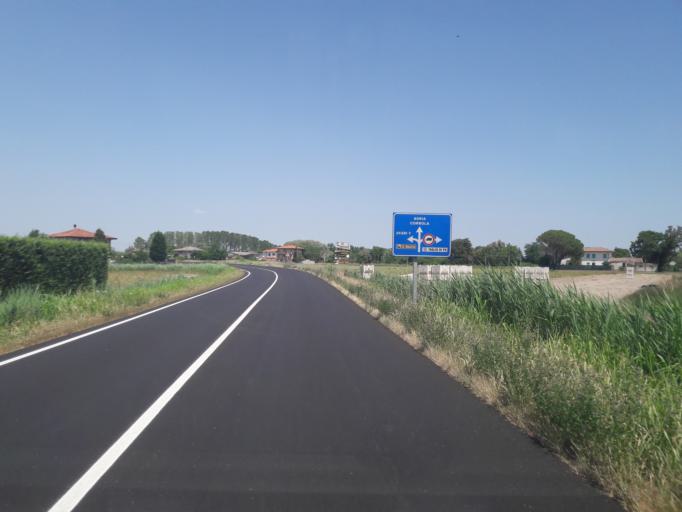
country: IT
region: Veneto
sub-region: Provincia di Rovigo
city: Taglio di Po
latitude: 45.0020
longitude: 12.2019
